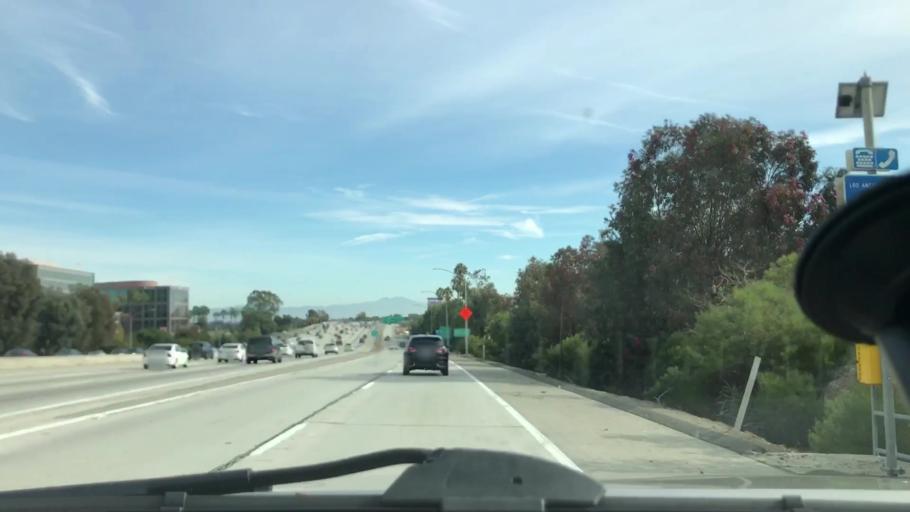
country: US
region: California
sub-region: Los Angeles County
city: Signal Hill
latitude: 33.8066
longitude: -118.1500
